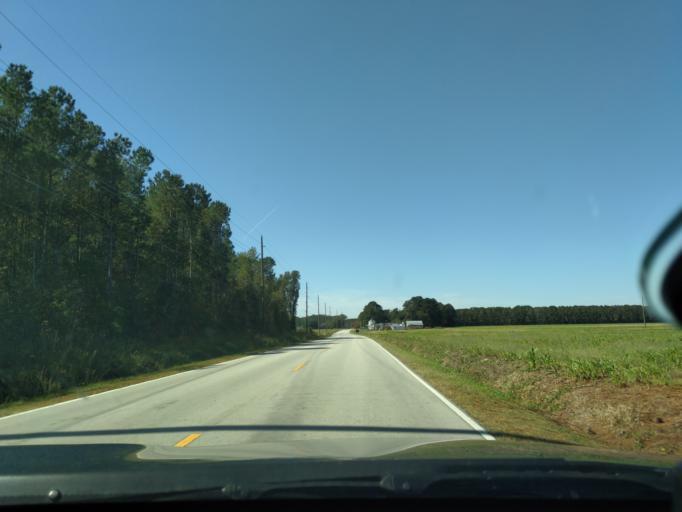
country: US
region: North Carolina
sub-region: Beaufort County
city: River Road
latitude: 35.5774
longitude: -76.9563
